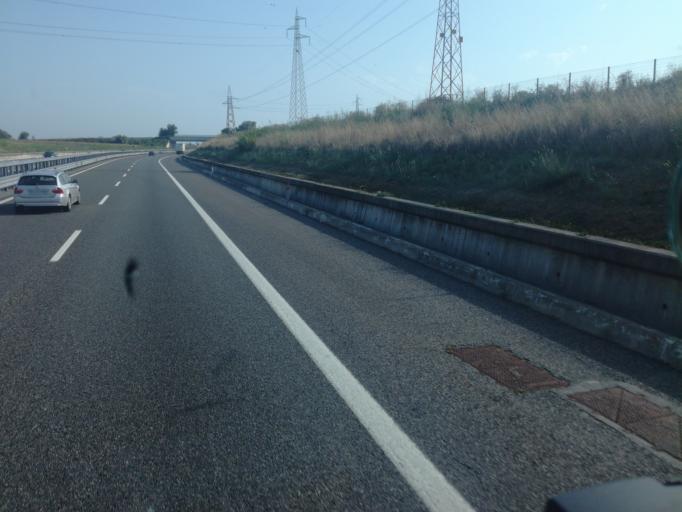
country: IT
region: Piedmont
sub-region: Provincia di Torino
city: Pasta
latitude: 44.9984
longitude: 7.5636
